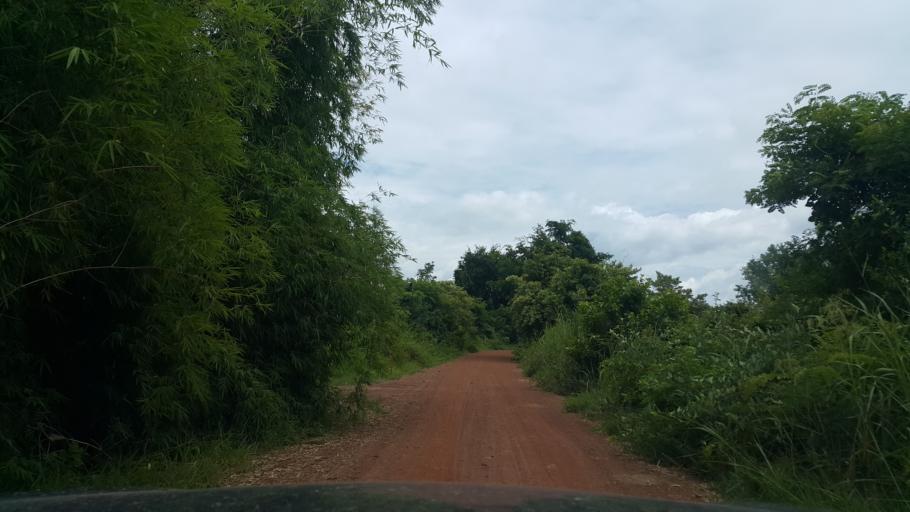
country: TH
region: Phitsanulok
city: Bang Rakam
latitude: 16.8402
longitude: 100.0644
